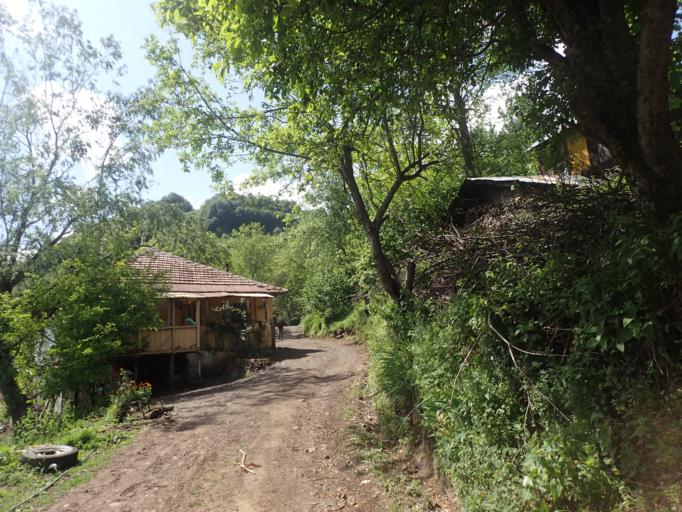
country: TR
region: Ordu
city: Akkus
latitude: 40.9054
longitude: 36.8810
